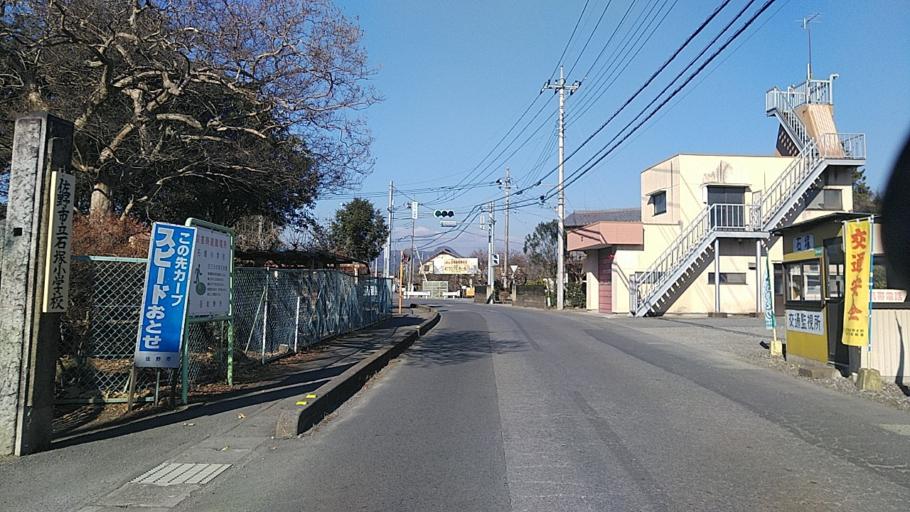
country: JP
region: Tochigi
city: Tanuma
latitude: 36.3551
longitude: 139.5624
